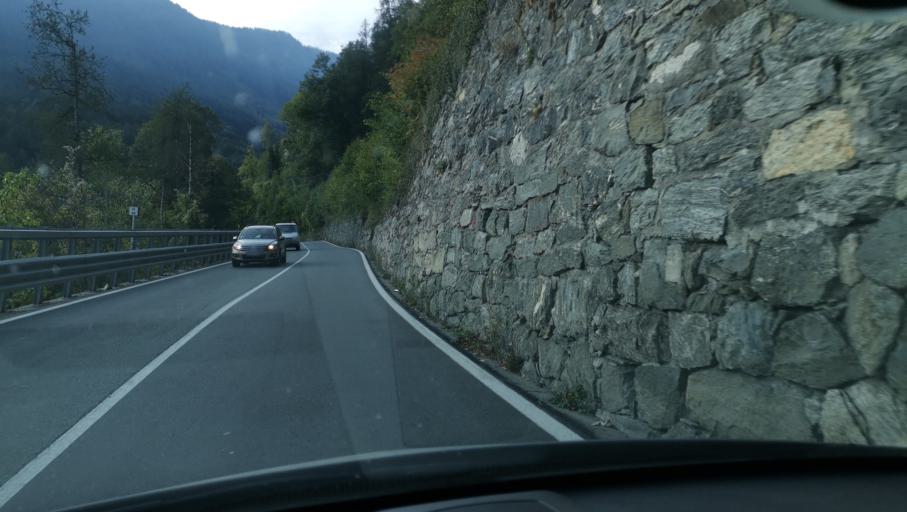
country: IT
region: Piedmont
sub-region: Provincia di Torino
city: Exilles
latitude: 45.0872
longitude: 6.9078
